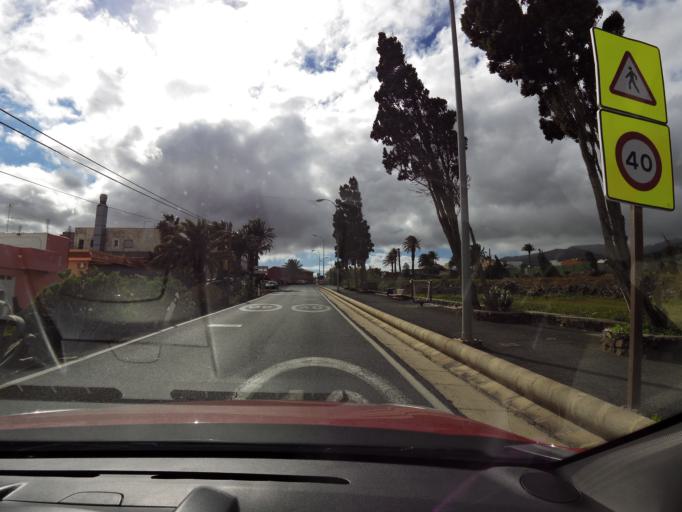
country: ES
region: Canary Islands
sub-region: Provincia de Las Palmas
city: Ingenio
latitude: 27.9266
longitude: -15.4301
